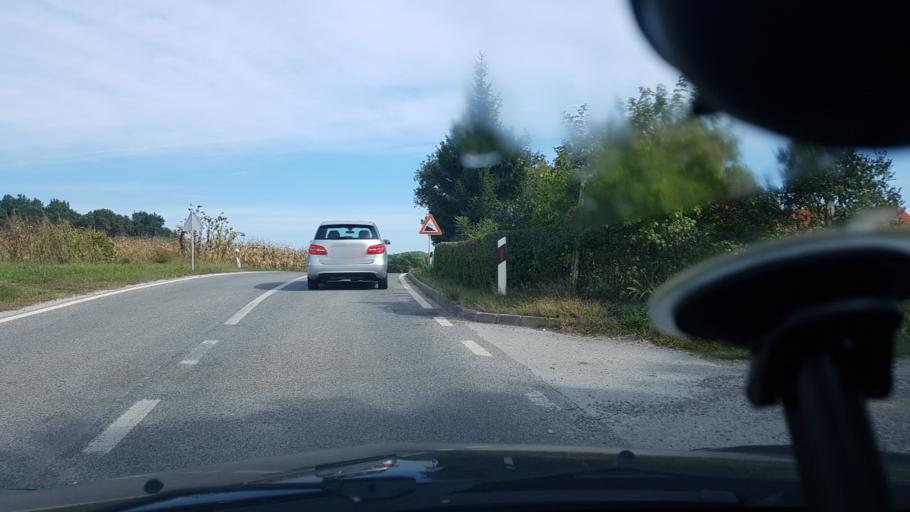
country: HR
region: Krapinsko-Zagorska
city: Marija Bistrica
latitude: 46.0809
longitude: 16.1971
